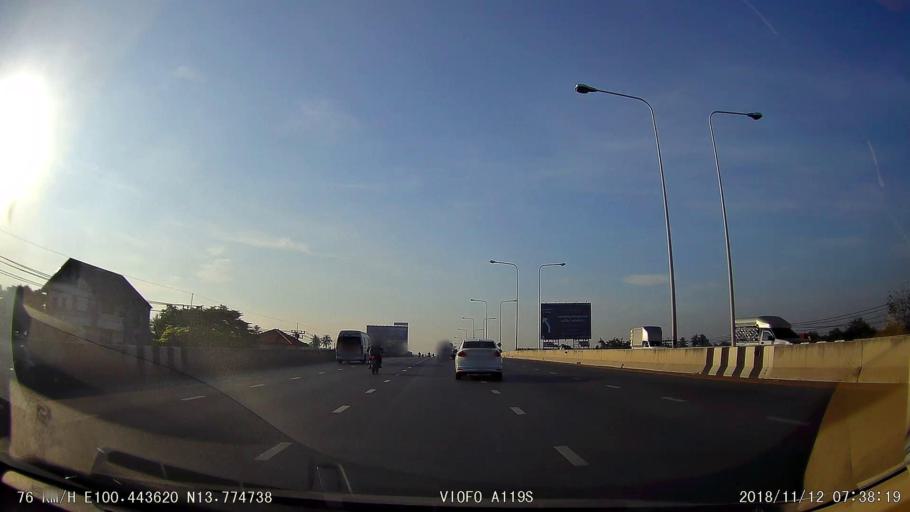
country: TH
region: Bangkok
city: Taling Chan
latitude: 13.7744
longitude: 100.4438
